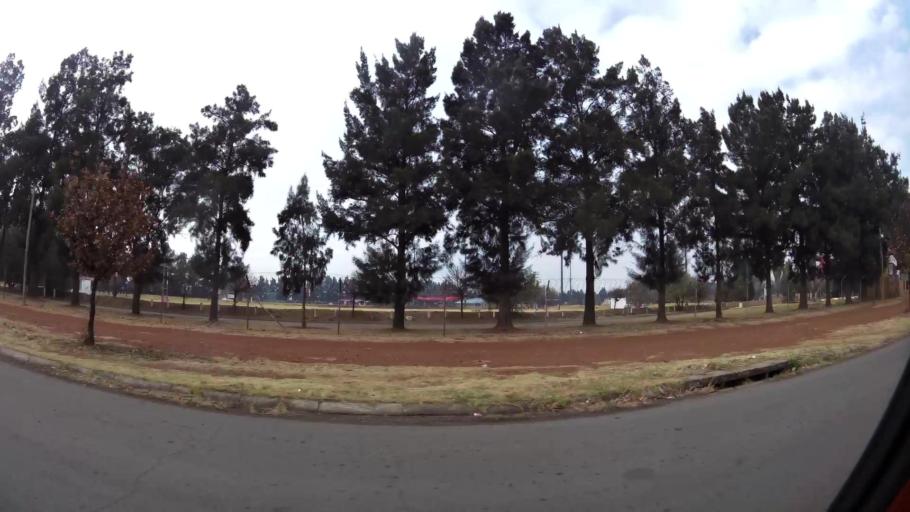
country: ZA
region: Gauteng
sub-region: Sedibeng District Municipality
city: Vanderbijlpark
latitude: -26.7031
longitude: 27.8596
